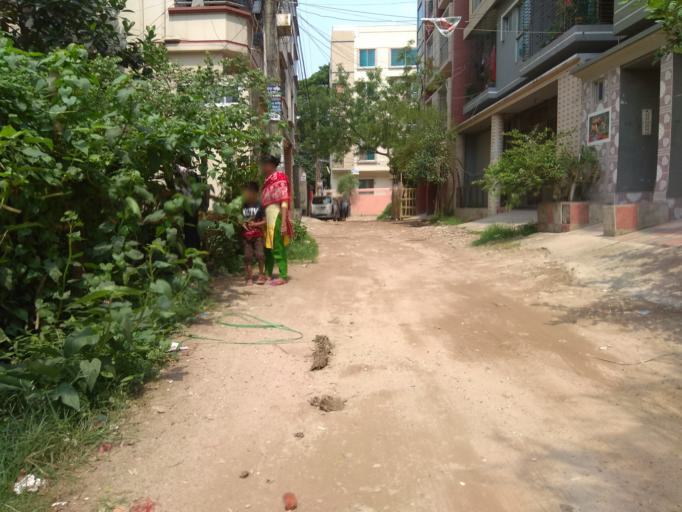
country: BD
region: Dhaka
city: Tungi
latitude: 23.8274
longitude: 90.3519
